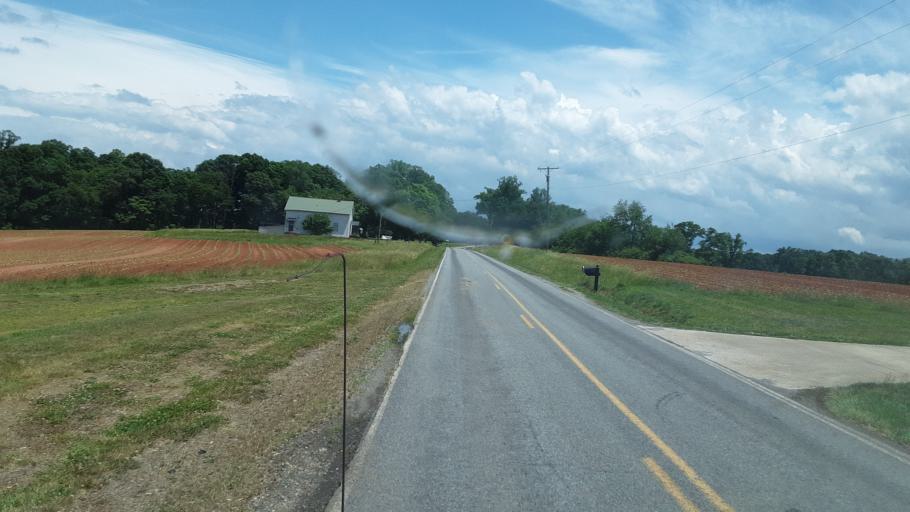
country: US
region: North Carolina
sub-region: Yadkin County
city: Jonesville
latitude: 36.0754
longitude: -80.8468
